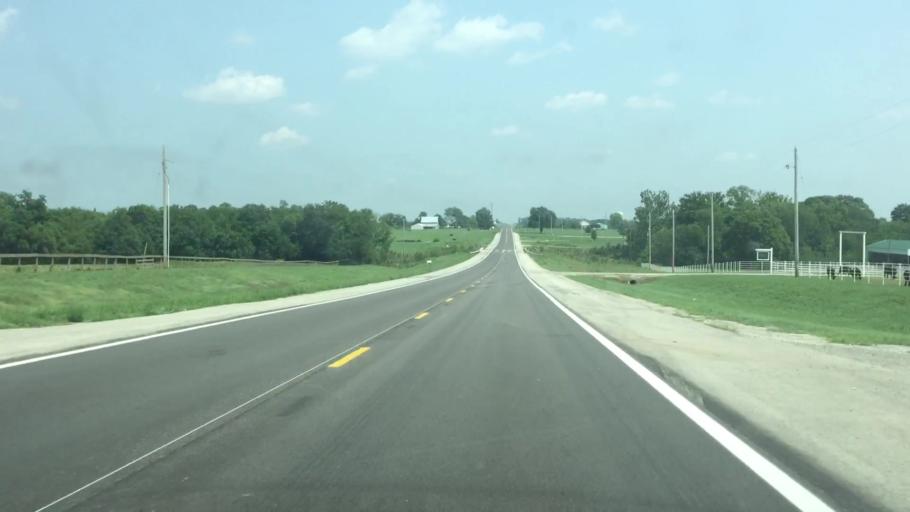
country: US
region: Kansas
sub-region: Douglas County
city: Baldwin City
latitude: 38.7822
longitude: -95.2361
